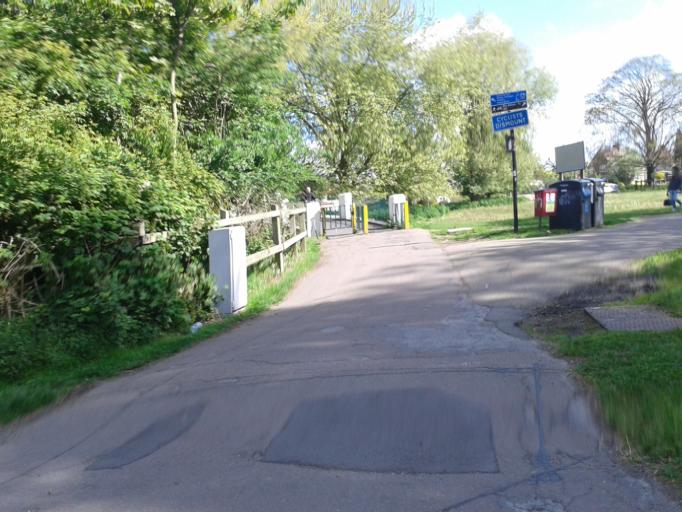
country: GB
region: England
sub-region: Cambridgeshire
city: Cambridge
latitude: 52.2168
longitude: 0.1462
